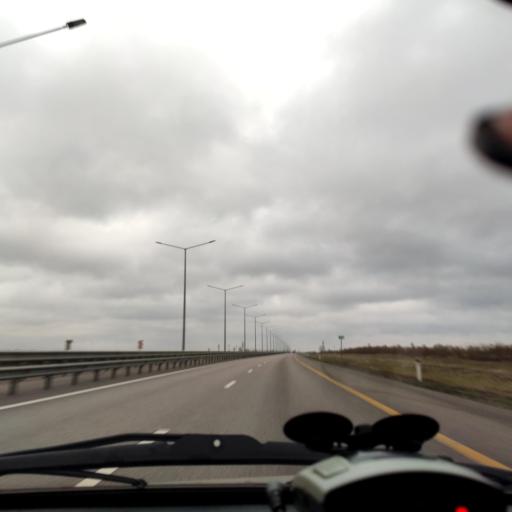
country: RU
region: Voronezj
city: Novaya Usman'
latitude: 51.6009
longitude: 39.3456
